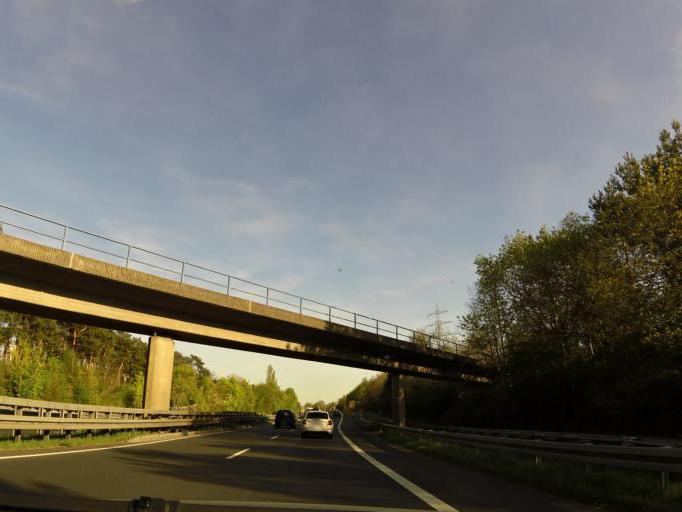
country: DE
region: Hesse
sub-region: Regierungsbezirk Darmstadt
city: Darmstadt
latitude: 49.8950
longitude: 8.6237
